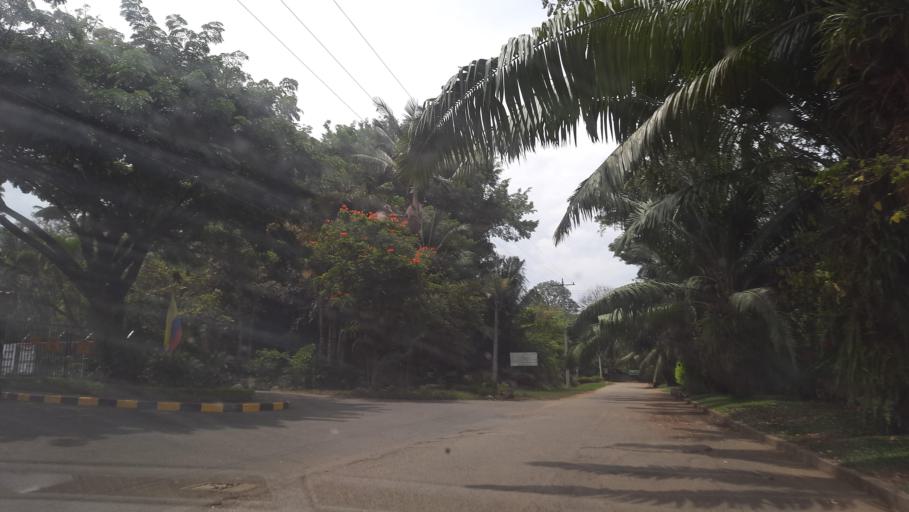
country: CO
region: Valle del Cauca
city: Jamundi
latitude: 3.2677
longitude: -76.5112
